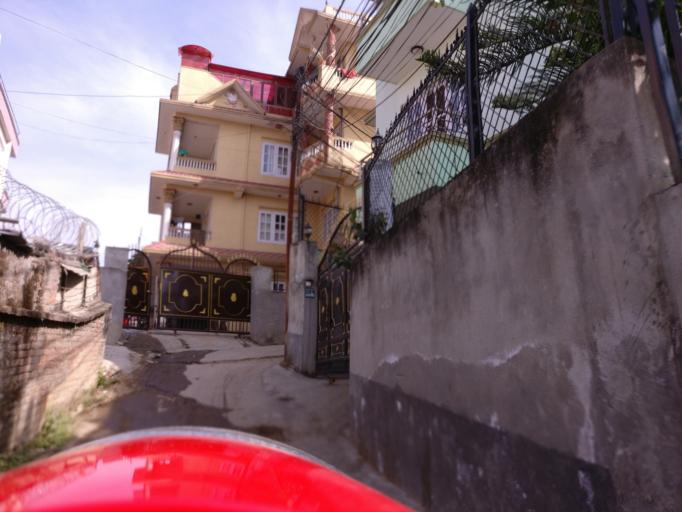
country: NP
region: Central Region
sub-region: Bagmati Zone
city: Patan
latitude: 27.6633
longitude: 85.3117
